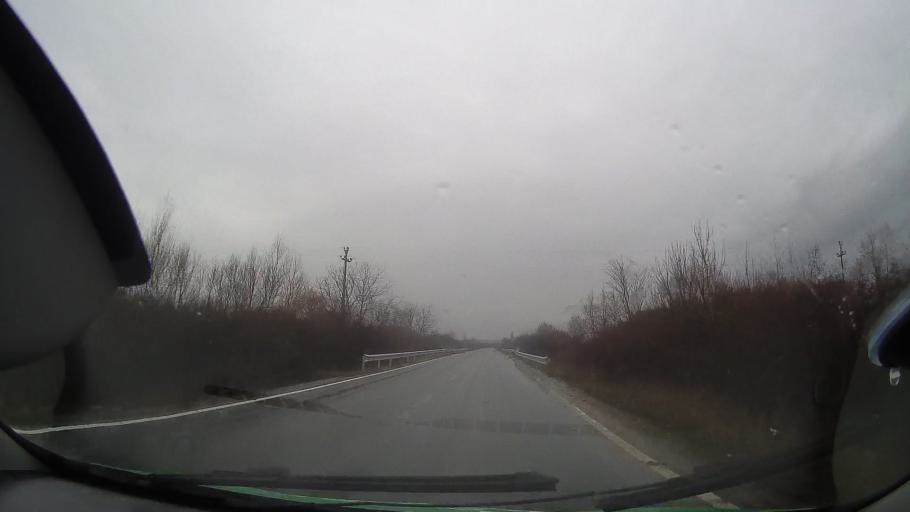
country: RO
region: Bihor
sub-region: Comuna Tinca
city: Tinca
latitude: 46.7408
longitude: 21.9404
